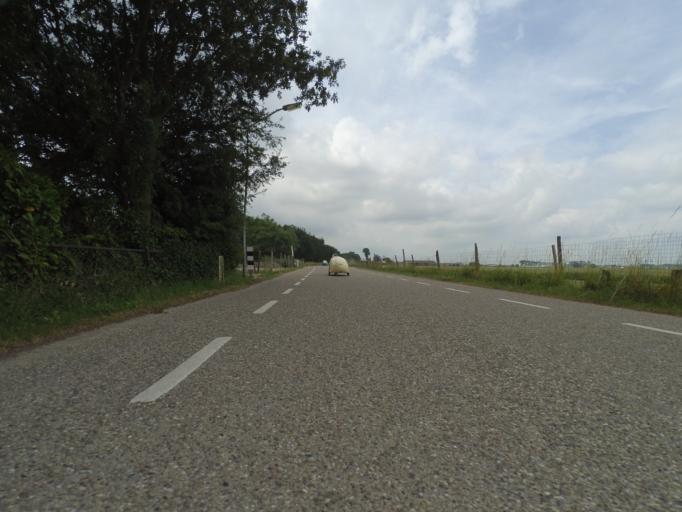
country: NL
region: North Brabant
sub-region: Gemeente Moerdijk
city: Klundert
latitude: 51.6425
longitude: 4.6551
